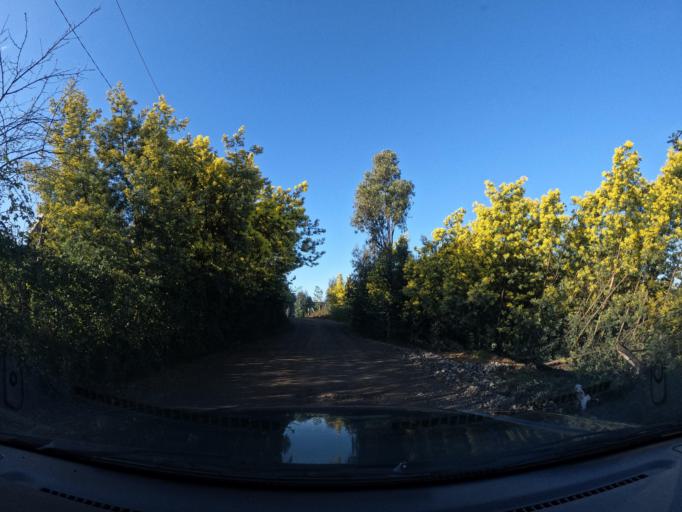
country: CL
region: Biobio
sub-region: Provincia de Concepcion
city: Chiguayante
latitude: -37.0143
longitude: -72.8481
